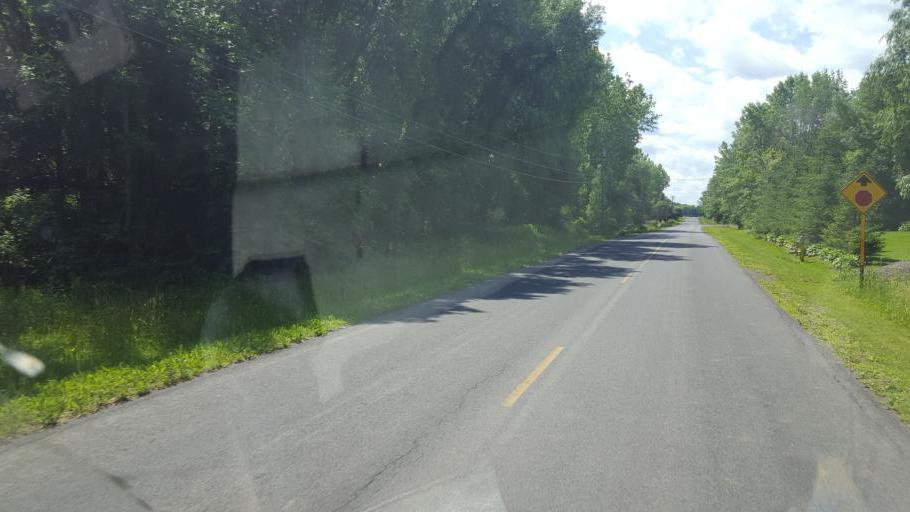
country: US
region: New York
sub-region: Wayne County
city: Wolcott
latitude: 43.2560
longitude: -76.9235
